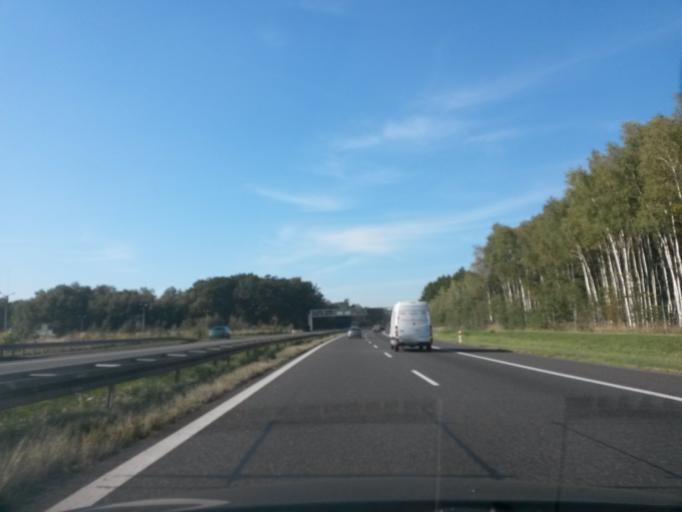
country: PL
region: Silesian Voivodeship
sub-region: Powiat gliwicki
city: Sosnicowice
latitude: 50.3519
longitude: 18.5269
